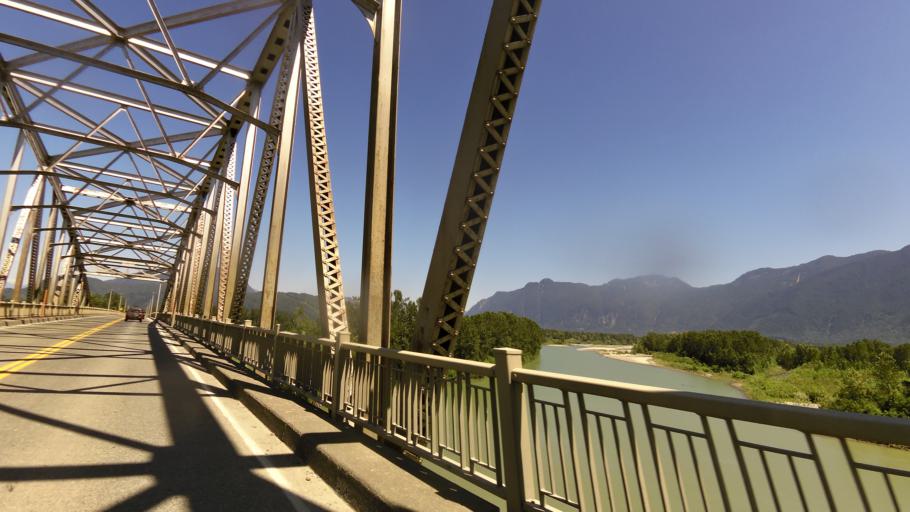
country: CA
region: British Columbia
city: Agassiz
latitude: 49.2066
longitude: -121.7769
